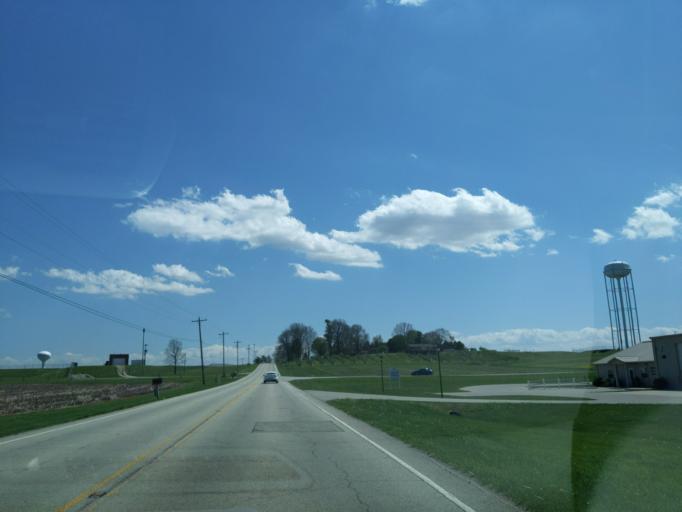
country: US
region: Indiana
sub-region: Decatur County
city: Greensburg
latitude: 39.3873
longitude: -85.5481
